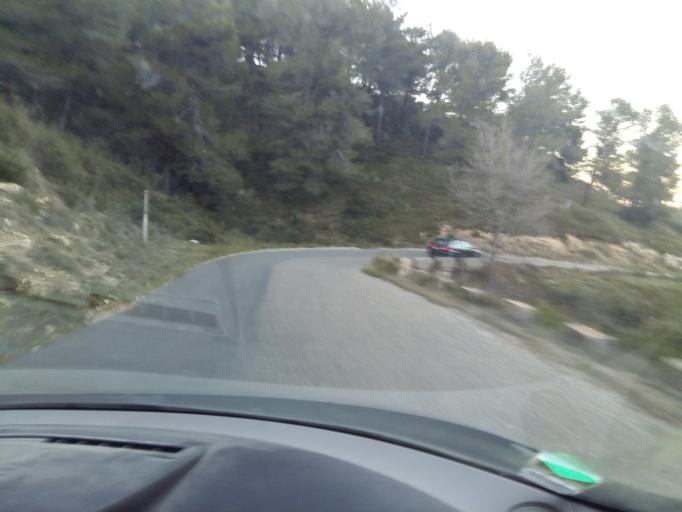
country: FR
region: Provence-Alpes-Cote d'Azur
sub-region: Departement des Bouches-du-Rhone
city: Maussane-les-Alpilles
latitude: 43.7545
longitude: 4.7924
